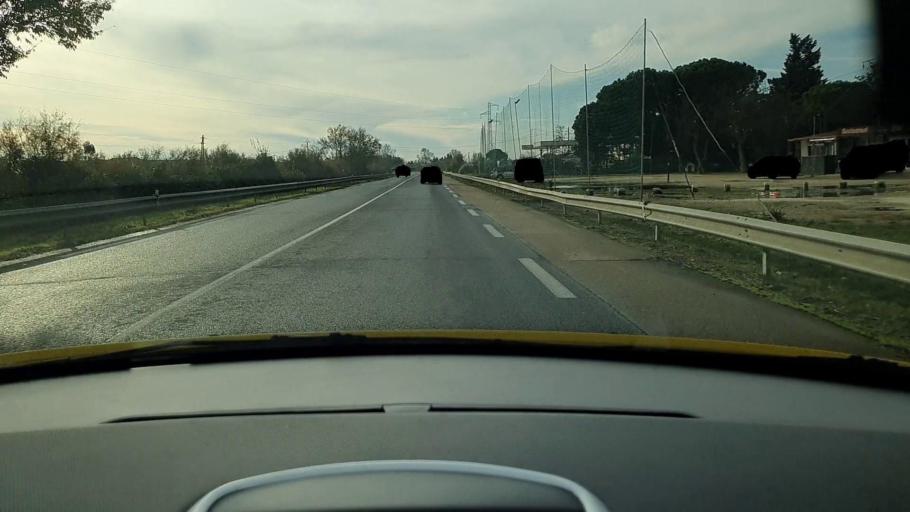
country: FR
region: Languedoc-Roussillon
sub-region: Departement du Gard
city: Bellegarde
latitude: 43.7384
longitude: 4.5220
